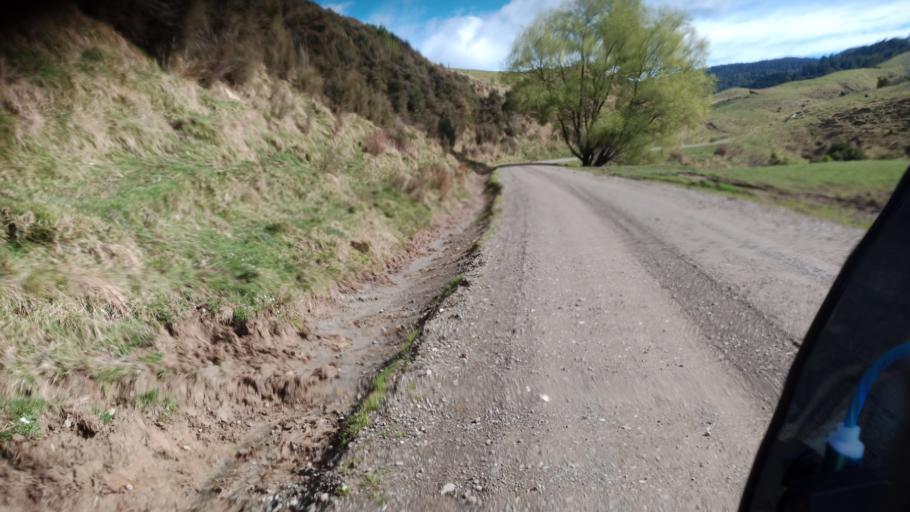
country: NZ
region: Hawke's Bay
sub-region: Wairoa District
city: Wairoa
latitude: -38.7357
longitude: 177.2989
